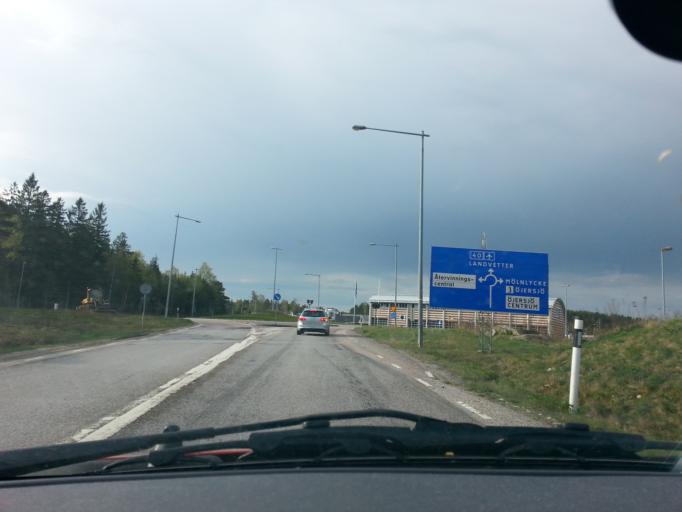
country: SE
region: Vaestra Goetaland
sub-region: Partille Kommun
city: Furulund
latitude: 57.7052
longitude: 12.1508
